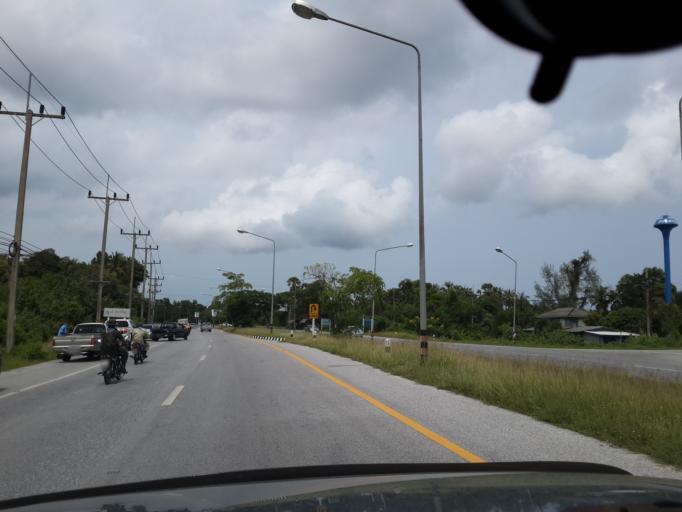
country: TH
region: Pattani
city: Yaring
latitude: 6.8554
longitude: 101.3763
